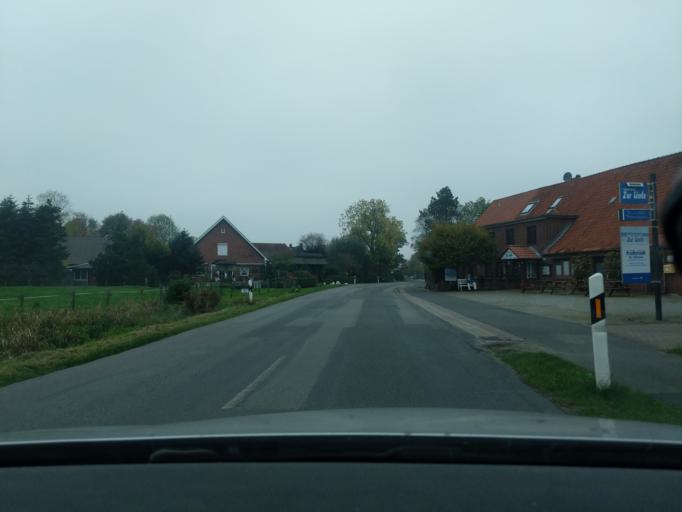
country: DE
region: Lower Saxony
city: Otterndorf
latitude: 53.8242
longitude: 8.8513
